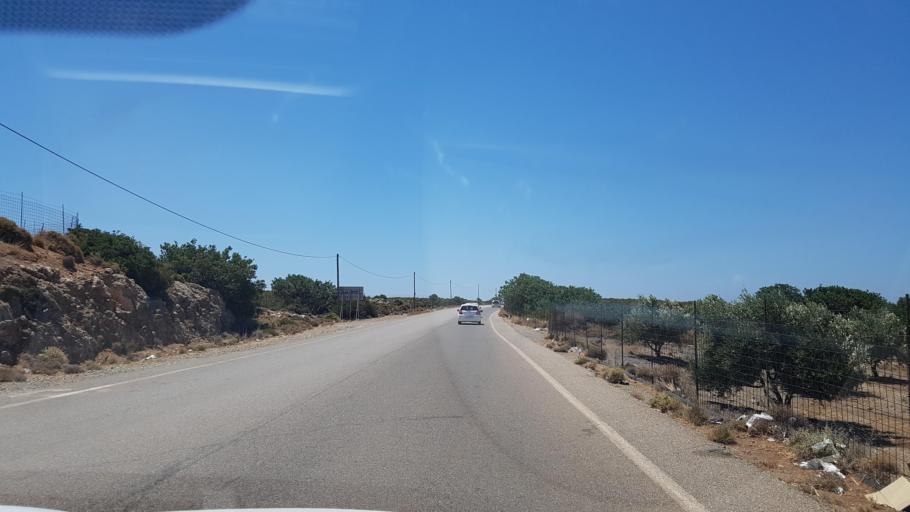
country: GR
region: Crete
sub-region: Nomos Chanias
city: Palaiochora
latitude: 35.2834
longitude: 23.5478
